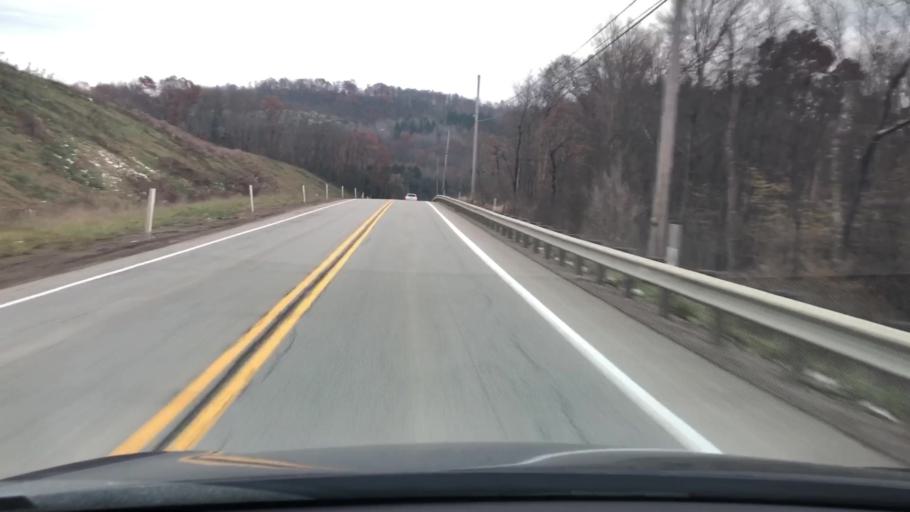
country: US
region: Pennsylvania
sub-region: Armstrong County
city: Kittanning
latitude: 40.8810
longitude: -79.3920
